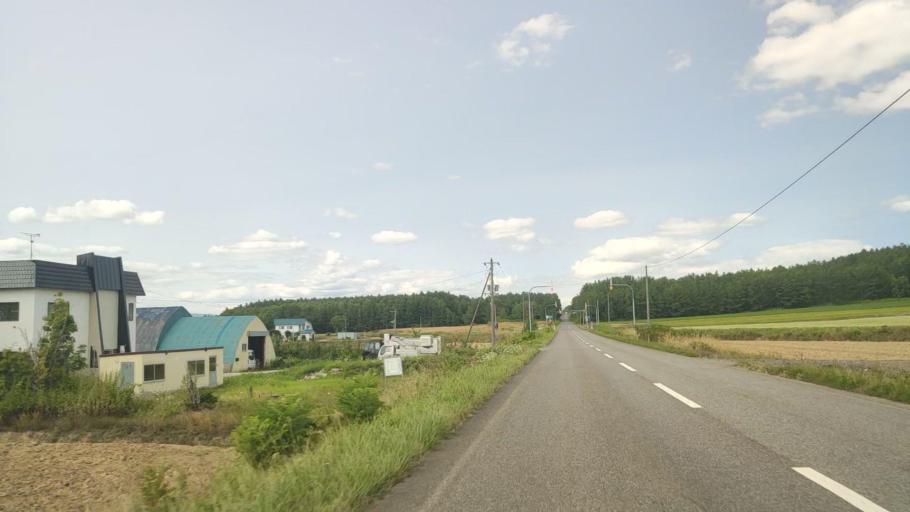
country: JP
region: Hokkaido
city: Nayoro
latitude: 44.2393
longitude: 142.4157
